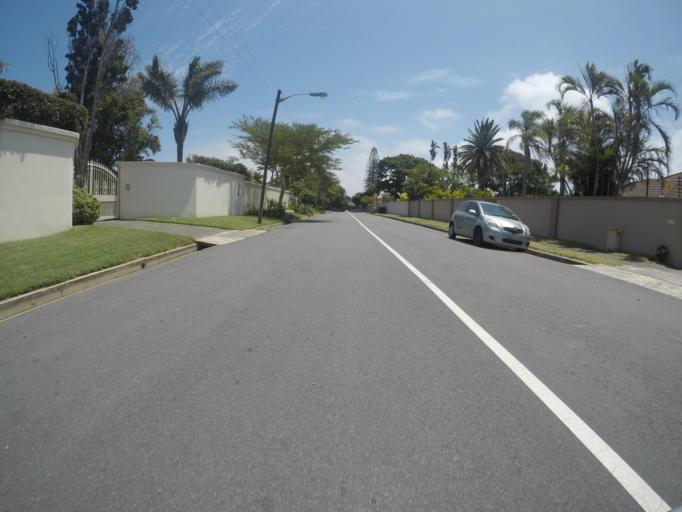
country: ZA
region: Eastern Cape
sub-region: Buffalo City Metropolitan Municipality
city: East London
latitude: -32.9967
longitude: 27.9272
